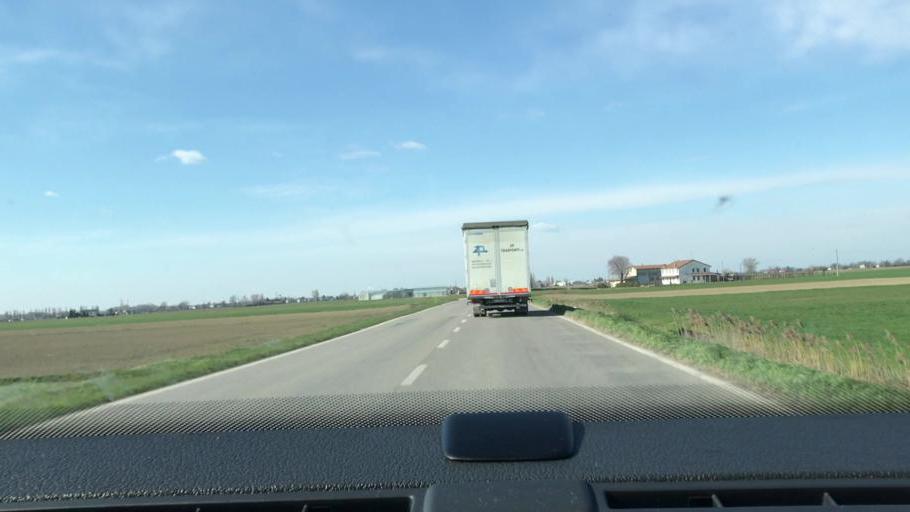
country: IT
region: Veneto
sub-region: Provincia di Rovigo
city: Calto
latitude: 44.9989
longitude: 11.3560
